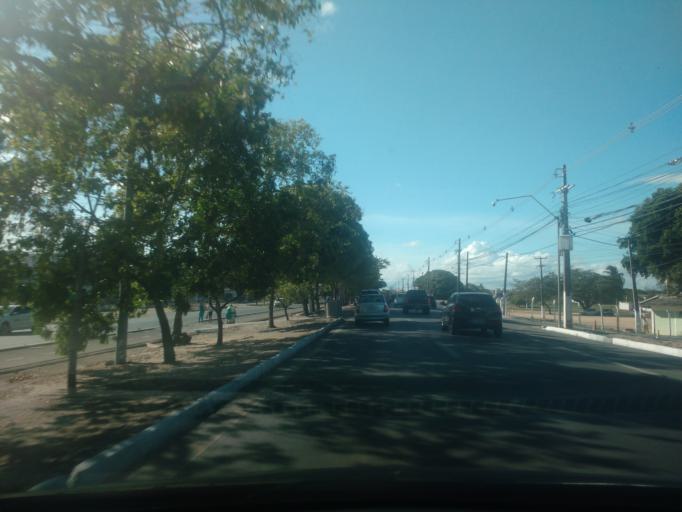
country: BR
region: Alagoas
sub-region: Satuba
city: Satuba
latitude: -9.5534
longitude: -35.7837
